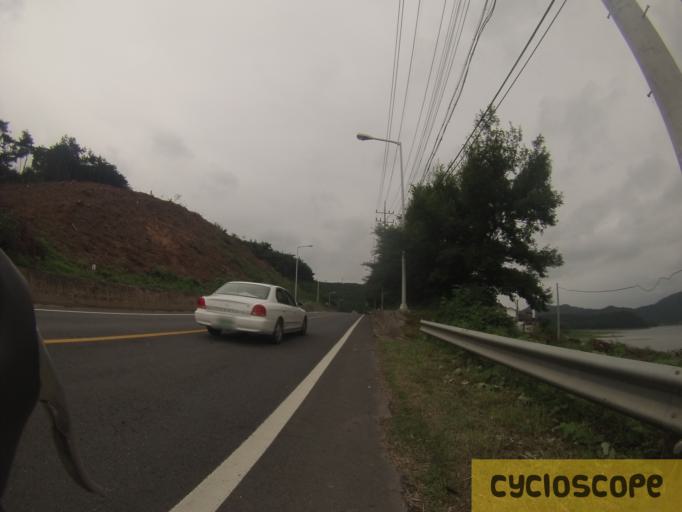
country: KR
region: Chungcheongnam-do
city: Taisen-ri
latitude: 36.4467
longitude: 126.7247
